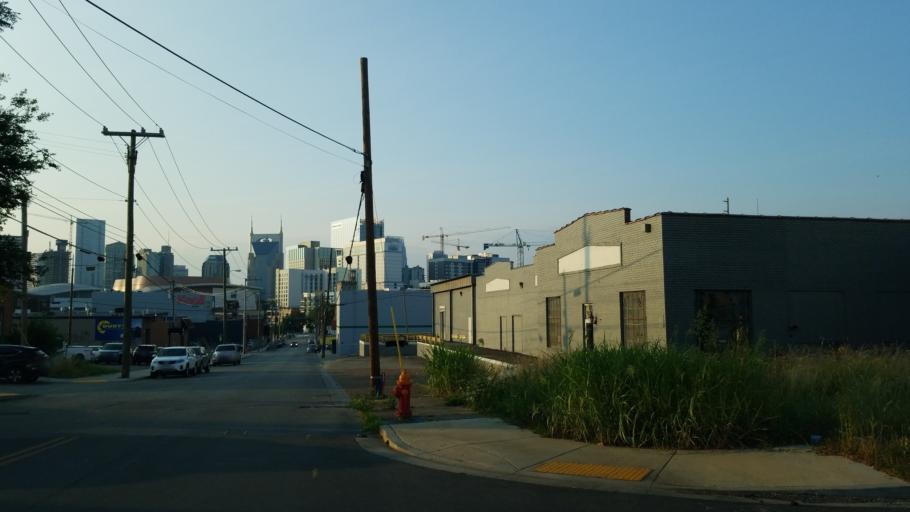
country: US
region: Tennessee
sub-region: Davidson County
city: Nashville
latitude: 36.1506
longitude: -86.7756
